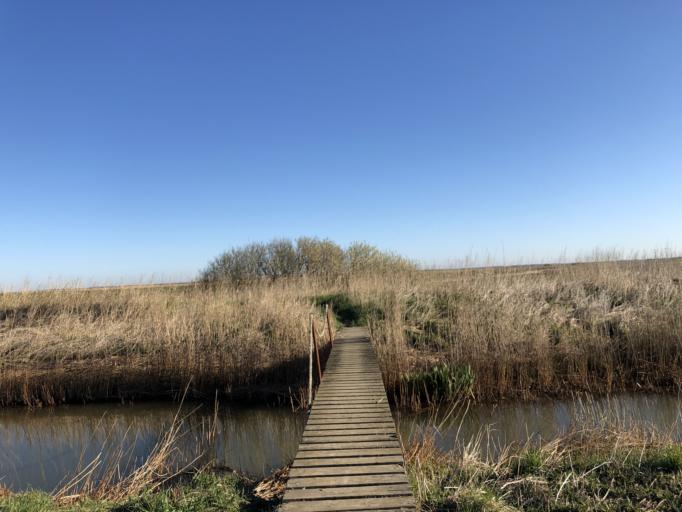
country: DK
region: Central Jutland
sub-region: Holstebro Kommune
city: Ulfborg
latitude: 56.2959
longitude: 8.2781
